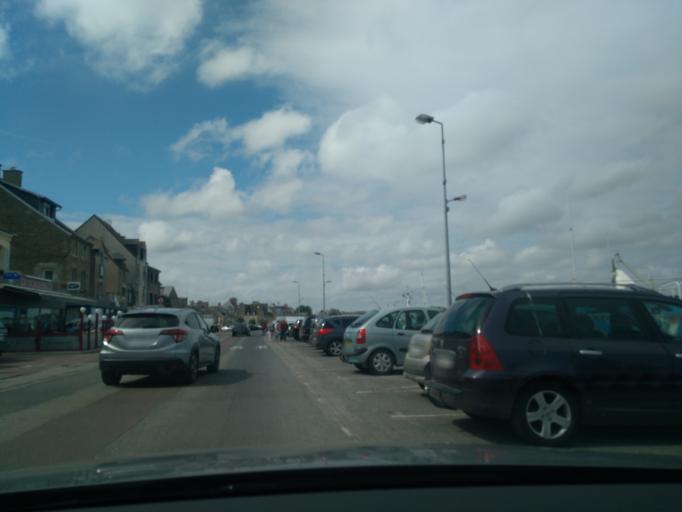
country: FR
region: Lower Normandy
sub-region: Departement de la Manche
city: Saint-Vaast-la-Hougue
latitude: 49.5874
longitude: -1.2651
